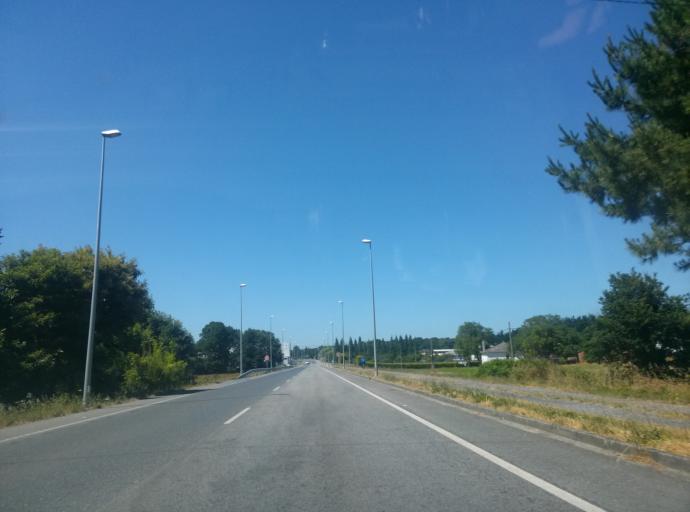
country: ES
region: Galicia
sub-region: Provincia de Lugo
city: Mos
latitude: 43.1311
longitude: -7.4887
